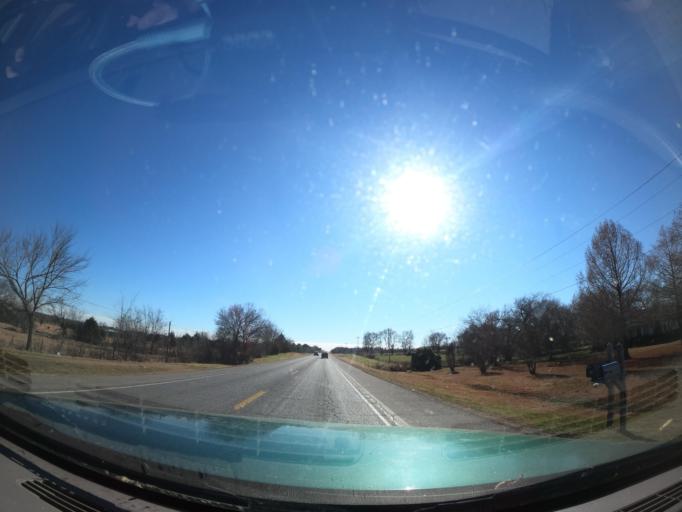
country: US
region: Oklahoma
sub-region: Muskogee County
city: Haskell
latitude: 35.8509
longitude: -95.6775
